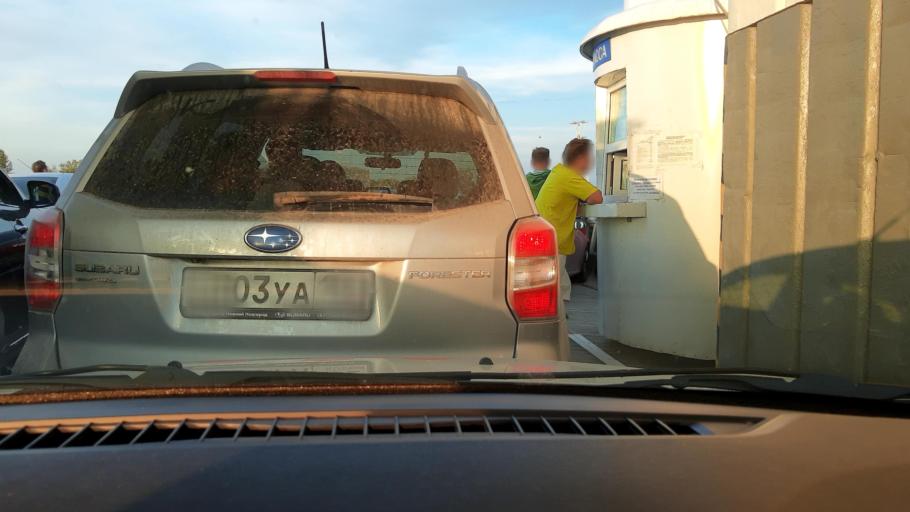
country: RU
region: Nizjnij Novgorod
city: Nizhniy Novgorod
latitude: 56.3396
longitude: 44.0383
